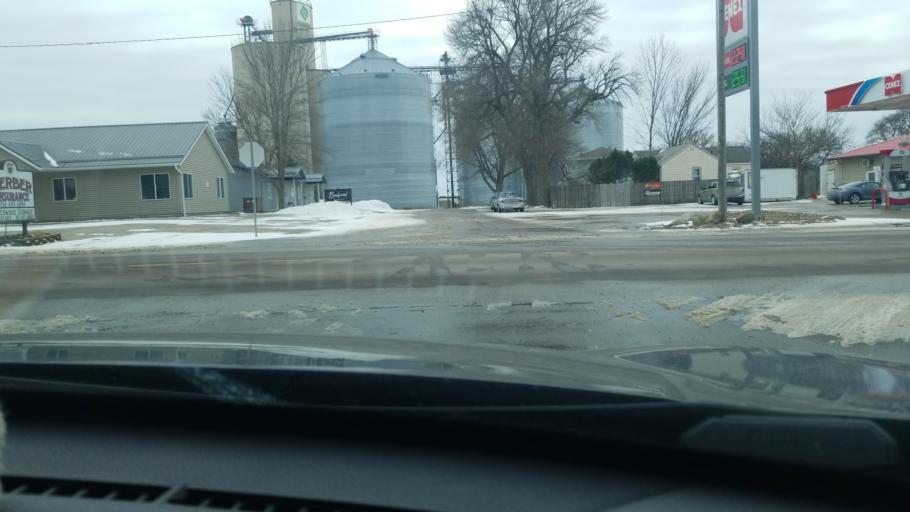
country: US
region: South Dakota
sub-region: Minnehaha County
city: Brandon
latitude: 43.4530
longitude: -96.4358
